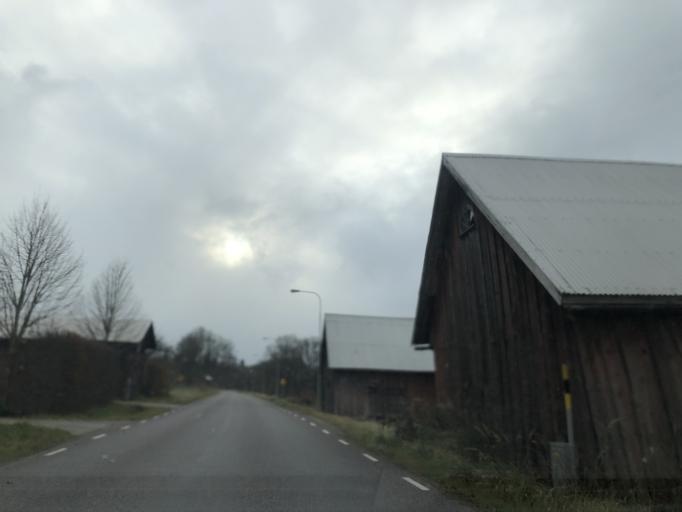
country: SE
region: Vaestra Goetaland
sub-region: Ulricehamns Kommun
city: Ulricehamn
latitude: 57.6827
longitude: 13.4142
